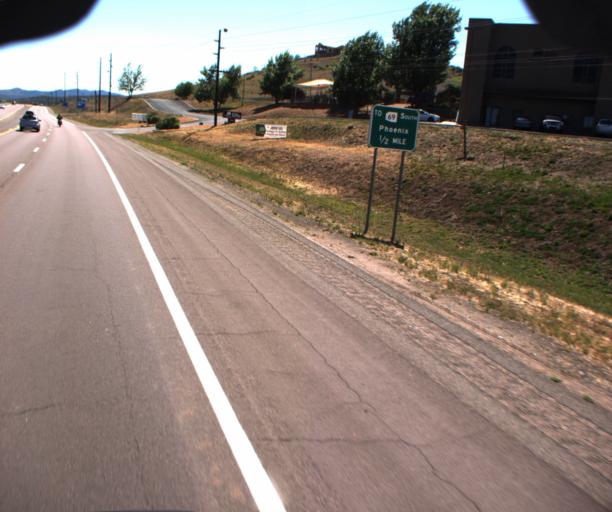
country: US
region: Arizona
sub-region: Yavapai County
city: Prescott
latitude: 34.5830
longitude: -112.4266
